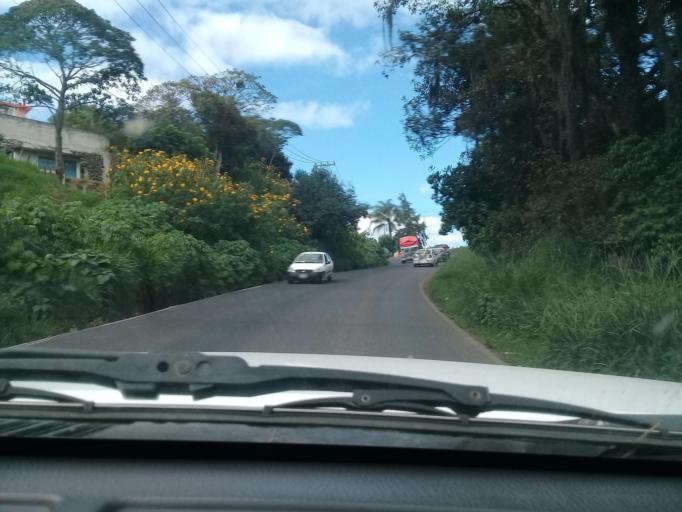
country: MX
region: Veracruz
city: El Castillo
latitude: 19.5470
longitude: -96.8862
